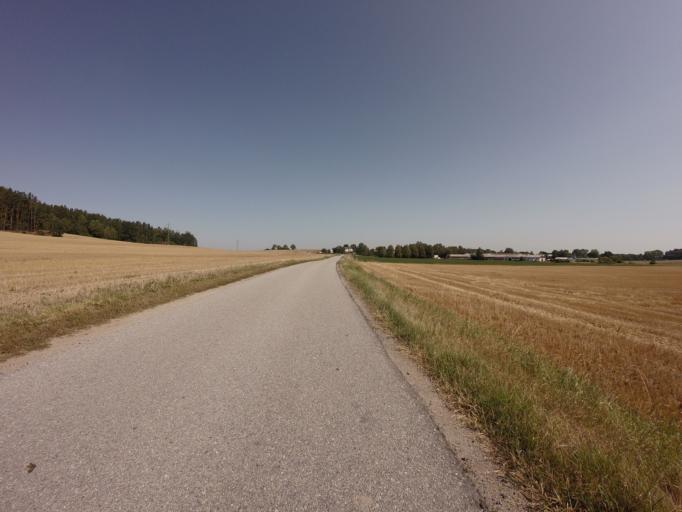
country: CZ
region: Jihocesky
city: Kamenny Ujezd
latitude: 48.8703
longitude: 14.3767
